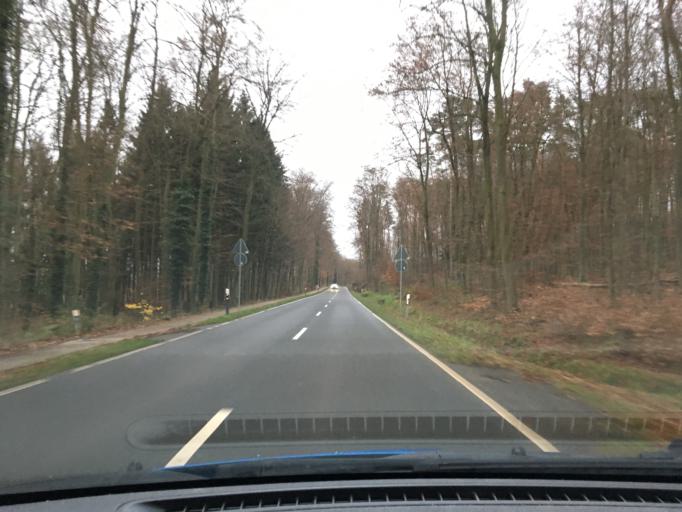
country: DE
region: Lower Saxony
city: Tosterglope
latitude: 53.2483
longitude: 10.8271
